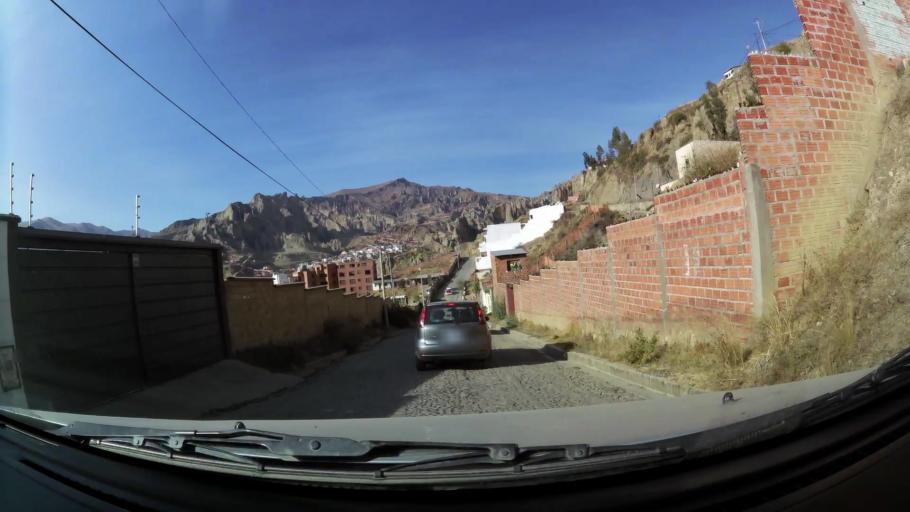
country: BO
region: La Paz
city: La Paz
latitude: -16.5075
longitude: -68.0833
